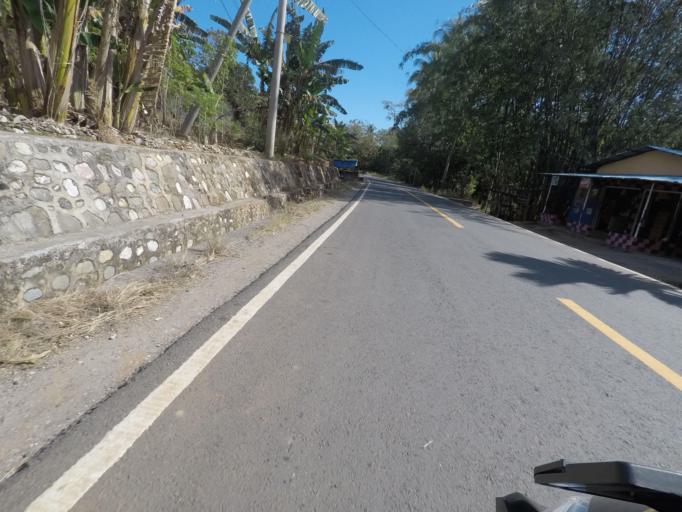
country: TL
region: Bobonaro
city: Maliana
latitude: -8.9541
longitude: 125.2119
